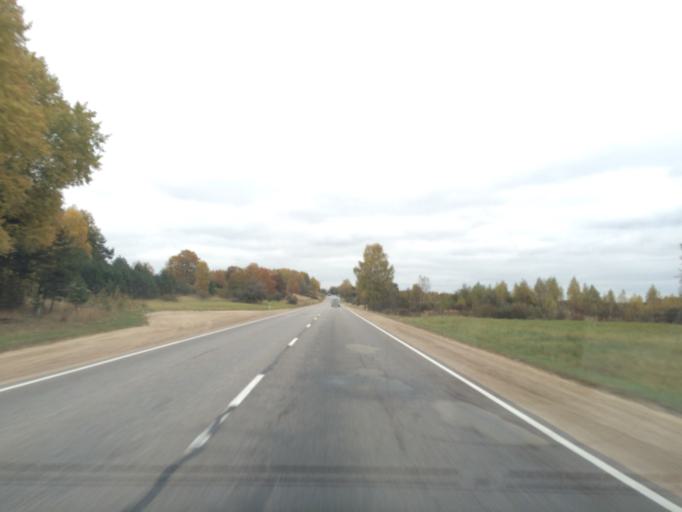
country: LV
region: Koknese
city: Koknese
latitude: 56.5963
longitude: 25.5355
